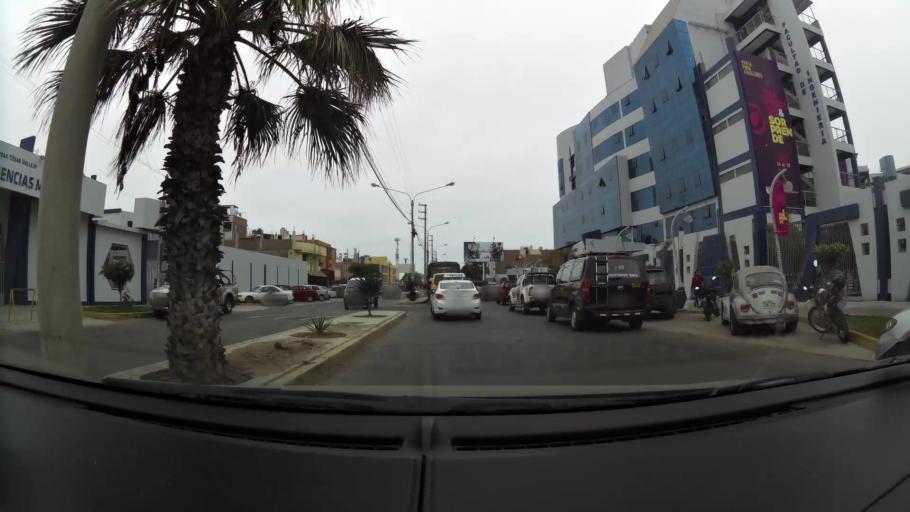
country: PE
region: La Libertad
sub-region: Provincia de Trujillo
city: Buenos Aires
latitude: -8.1297
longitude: -79.0433
